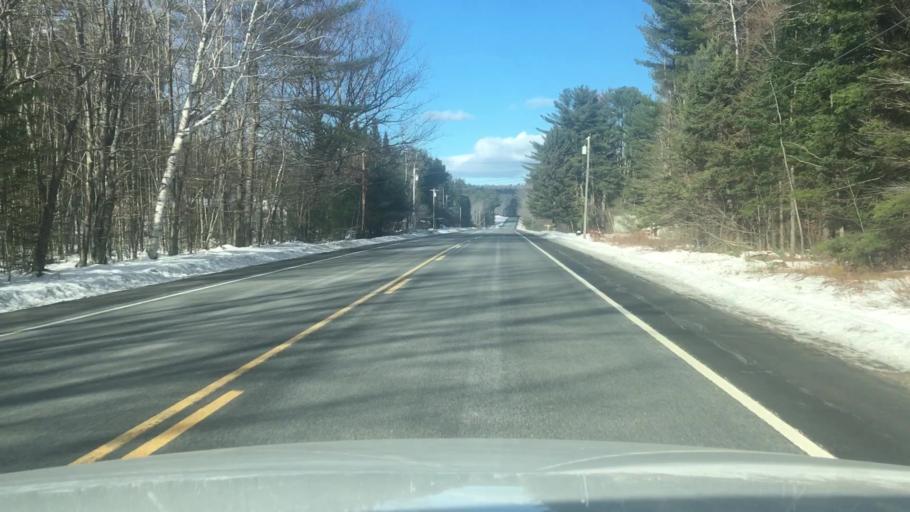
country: US
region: Maine
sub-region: Somerset County
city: Madison
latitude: 44.8518
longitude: -69.7922
